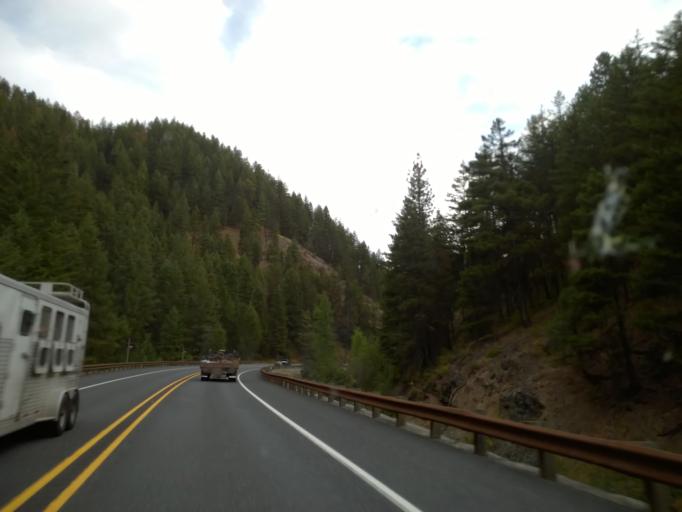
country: US
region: Washington
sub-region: Chelan County
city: Leavenworth
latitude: 47.4290
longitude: -120.6560
